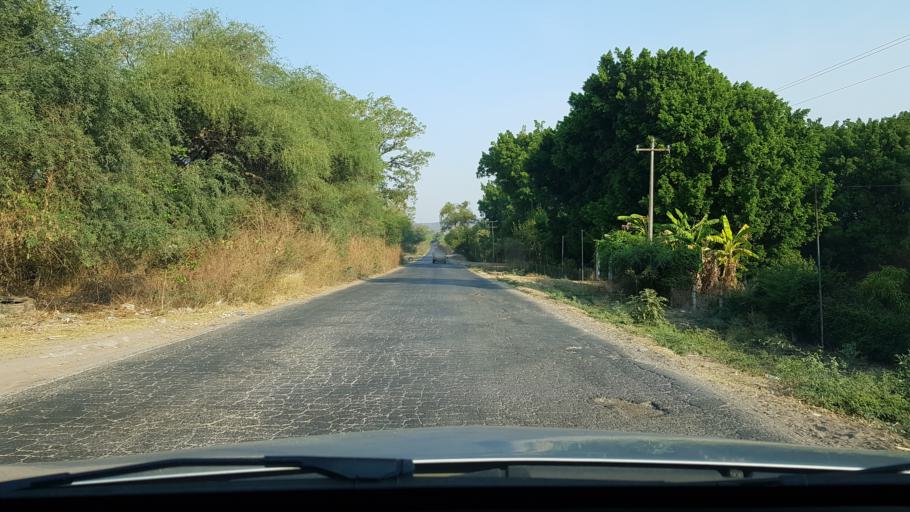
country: MX
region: Morelos
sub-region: Tepalcingo
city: Zacapalco
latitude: 18.6444
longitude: -99.0219
